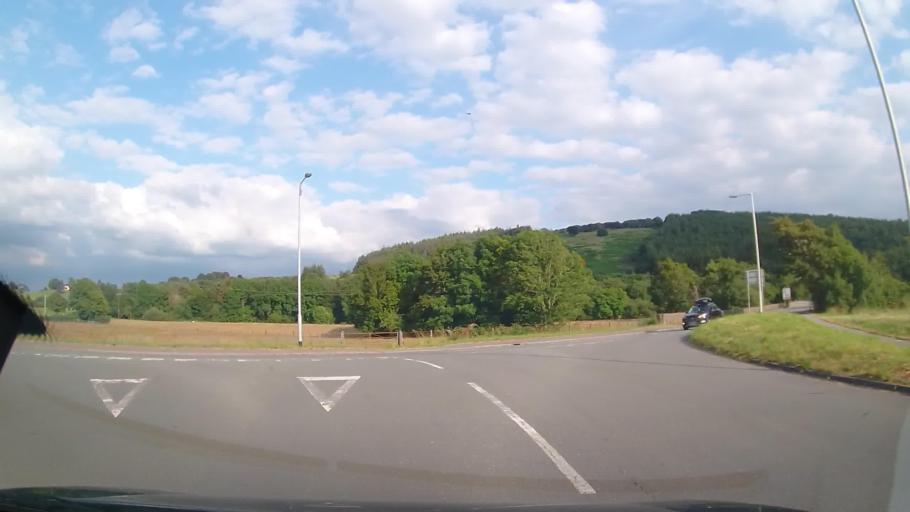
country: GB
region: Wales
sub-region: Gwynedd
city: Bala
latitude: 52.9043
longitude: -3.5936
